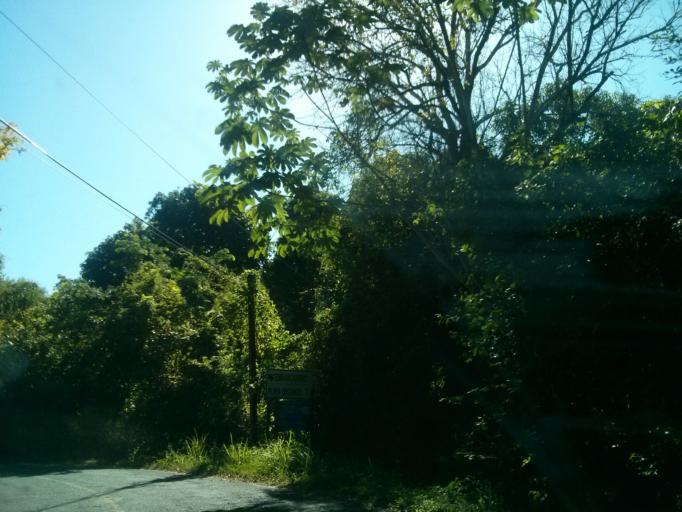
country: CR
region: Puntarenas
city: Paquera
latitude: 9.8227
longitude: -84.9146
